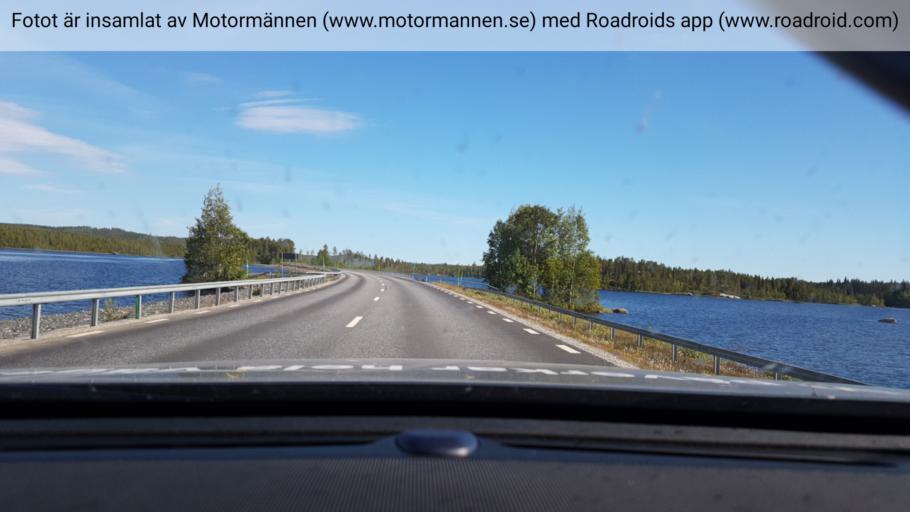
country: SE
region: Vaesterbotten
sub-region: Lycksele Kommun
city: Soderfors
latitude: 64.7553
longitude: 18.1728
